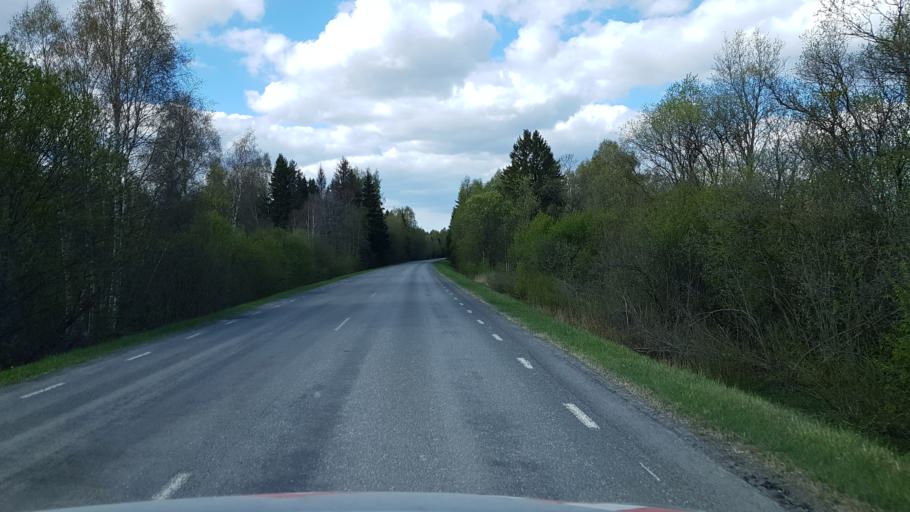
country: EE
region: Harju
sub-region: Keila linn
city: Keila
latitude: 59.2478
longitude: 24.4585
